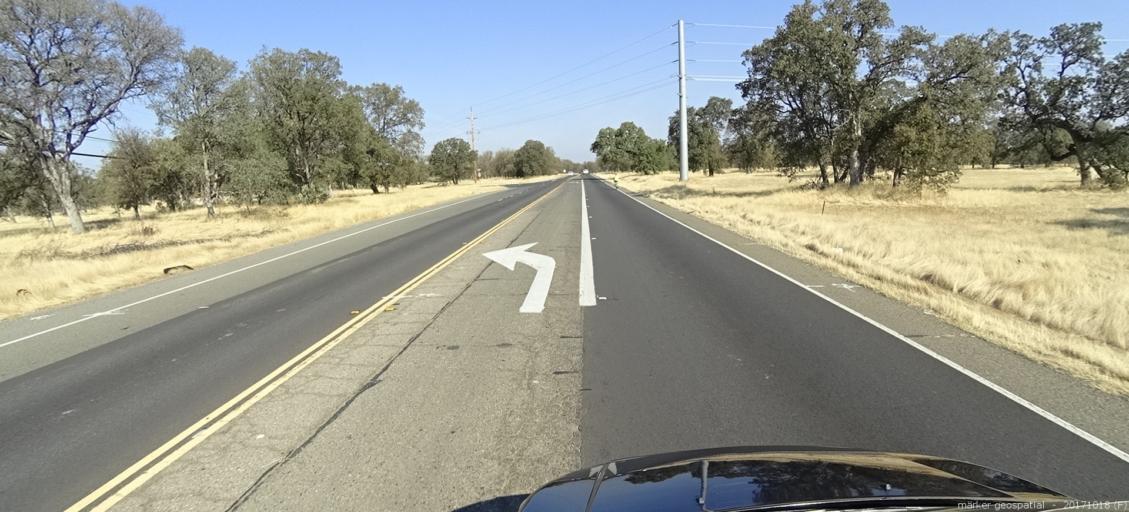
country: US
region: California
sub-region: Shasta County
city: Palo Cedro
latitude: 40.5532
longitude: -122.3028
